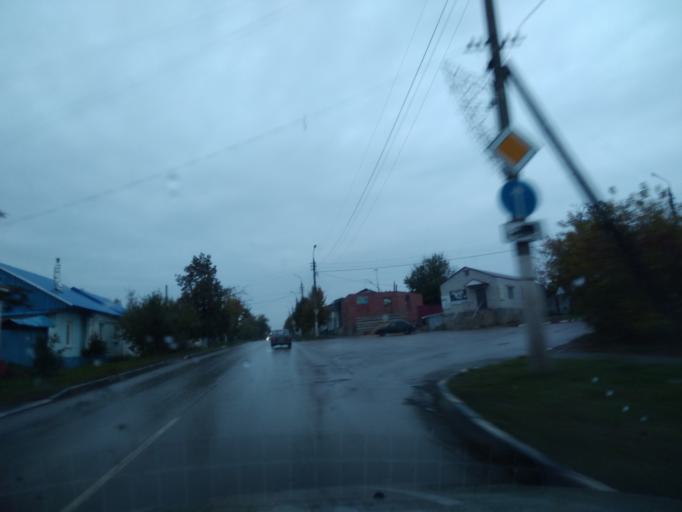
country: RU
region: Tula
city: Yefremov
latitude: 53.1383
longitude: 38.1149
